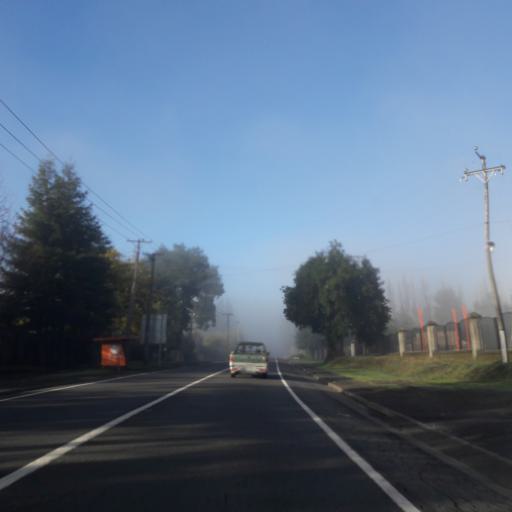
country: CL
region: Biobio
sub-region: Provincia de Concepcion
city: Chiguayante
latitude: -37.0149
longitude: -72.9873
